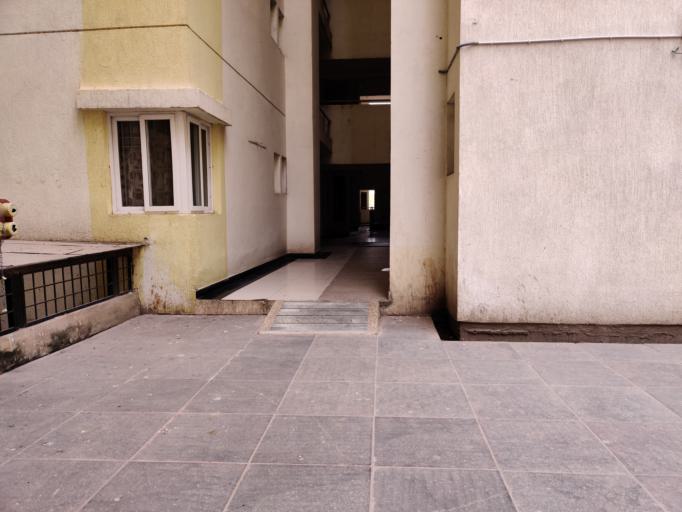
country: IN
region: Telangana
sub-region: Medak
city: Serilingampalle
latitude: 17.4233
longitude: 78.3408
